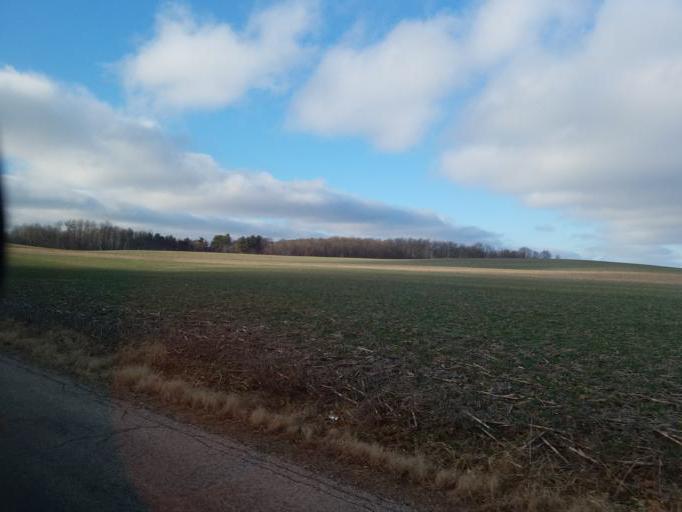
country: US
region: Ohio
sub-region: Ashland County
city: Loudonville
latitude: 40.6092
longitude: -82.3648
